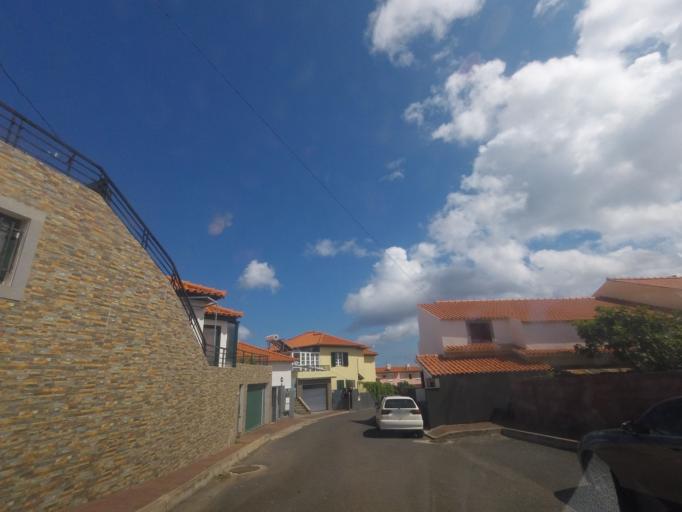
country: PT
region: Madeira
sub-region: Machico
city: Canical
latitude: 32.7389
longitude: -16.7391
